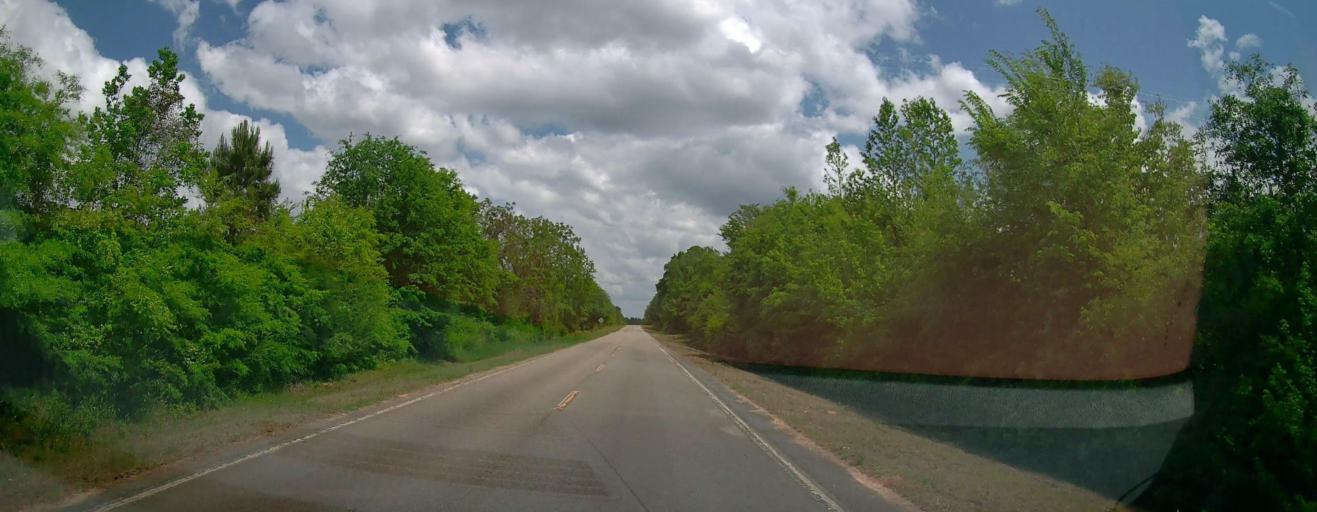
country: US
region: Georgia
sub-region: Dodge County
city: Chester
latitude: 32.5272
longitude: -83.2084
